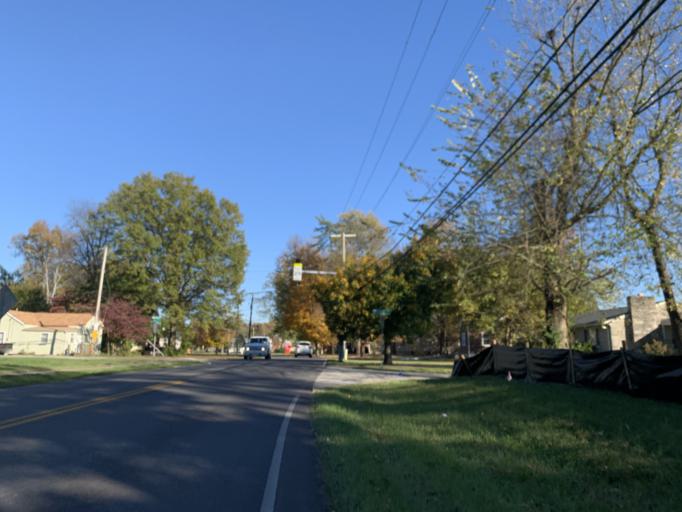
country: US
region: Kentucky
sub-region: Jefferson County
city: Saint Dennis
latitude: 38.1671
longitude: -85.8401
